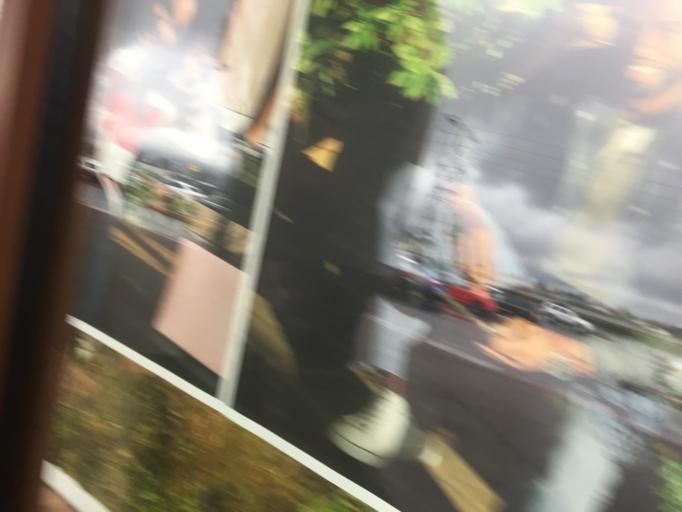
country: US
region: Oregon
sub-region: Marion County
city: Woodburn
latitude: 45.1551
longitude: -122.8788
